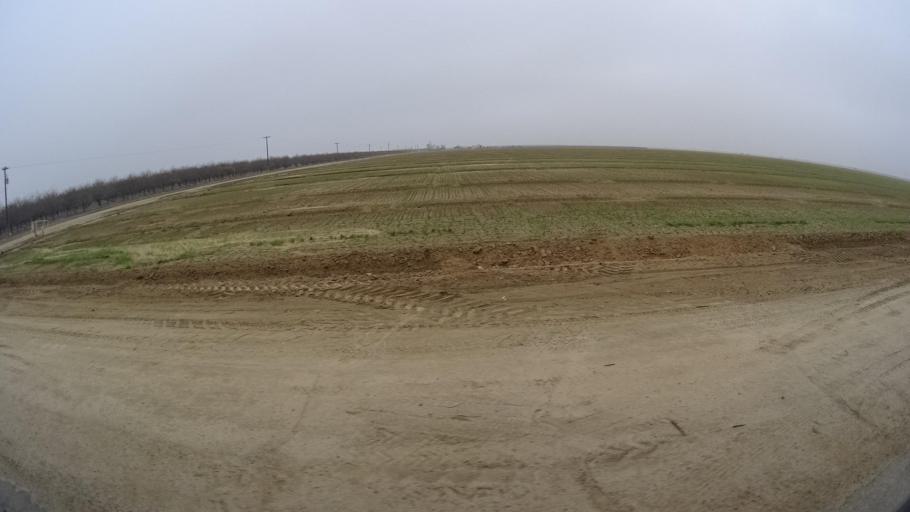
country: US
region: California
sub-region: Kern County
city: Lost Hills
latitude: 35.5870
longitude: -119.5270
